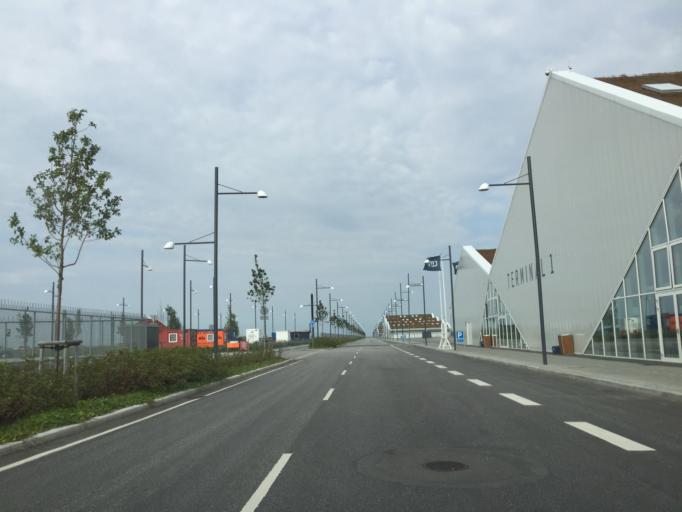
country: DK
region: Capital Region
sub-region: Kobenhavn
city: Christianshavn
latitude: 55.7135
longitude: 12.6189
